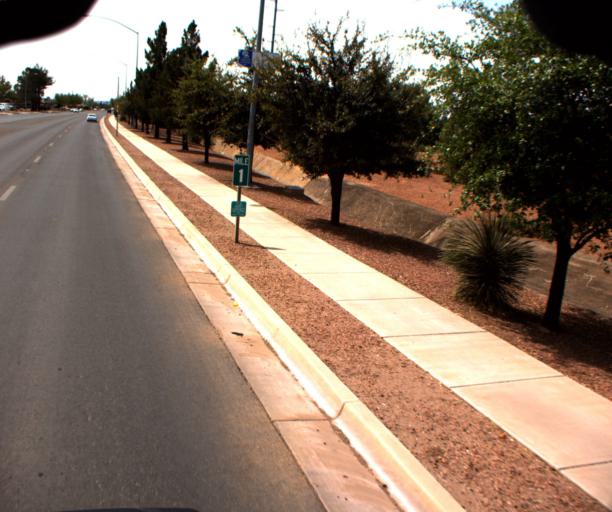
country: US
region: Arizona
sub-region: Cochise County
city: Douglas
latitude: 31.3481
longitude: -109.5559
